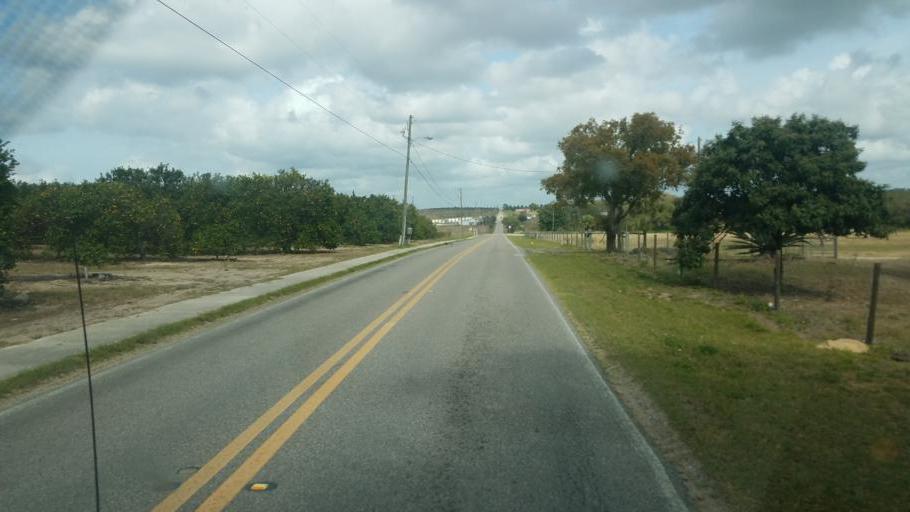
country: US
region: Florida
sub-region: Polk County
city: Dundee
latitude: 28.0314
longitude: -81.6115
